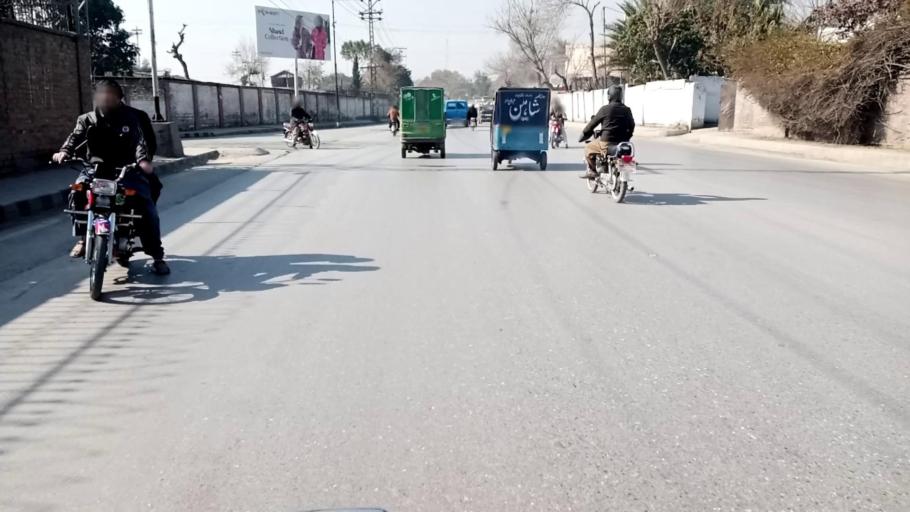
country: PK
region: Khyber Pakhtunkhwa
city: Peshawar
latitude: 34.0069
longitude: 71.5563
